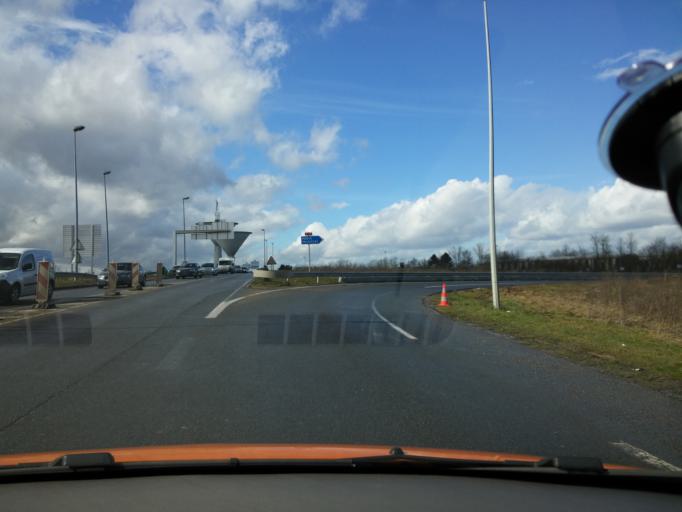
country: FR
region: Ile-de-France
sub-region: Departement de l'Essonne
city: Villejust
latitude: 48.6856
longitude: 2.2163
